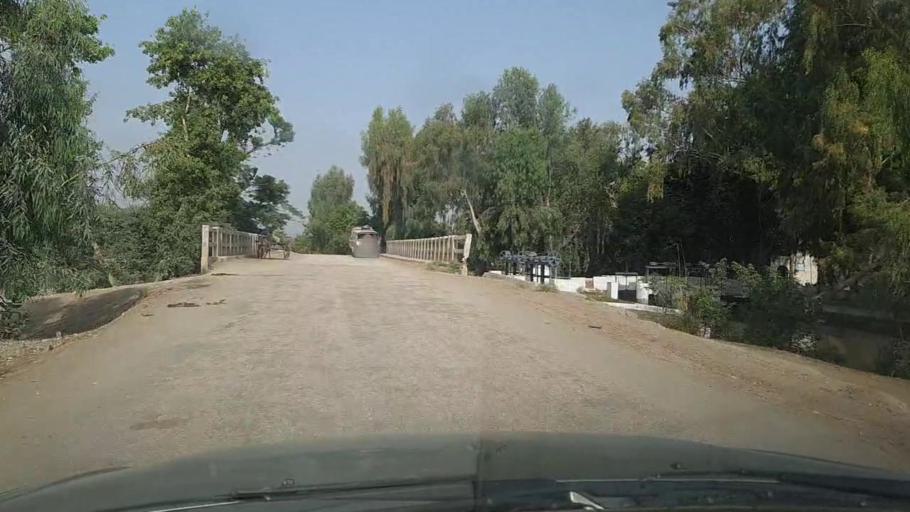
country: PK
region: Sindh
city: Pir jo Goth
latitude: 27.5160
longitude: 68.4730
